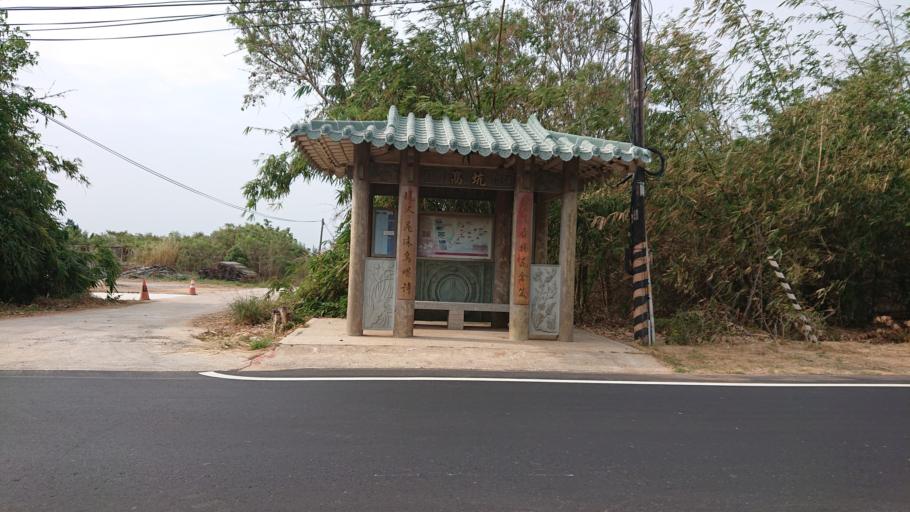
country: TW
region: Fukien
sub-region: Kinmen
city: Jincheng
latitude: 24.4663
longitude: 118.3884
